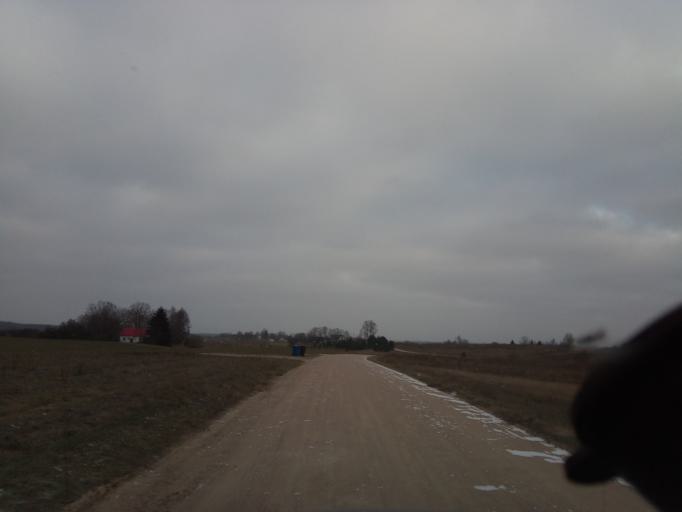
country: LT
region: Alytaus apskritis
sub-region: Alytaus rajonas
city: Daugai
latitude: 54.3781
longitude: 24.4366
